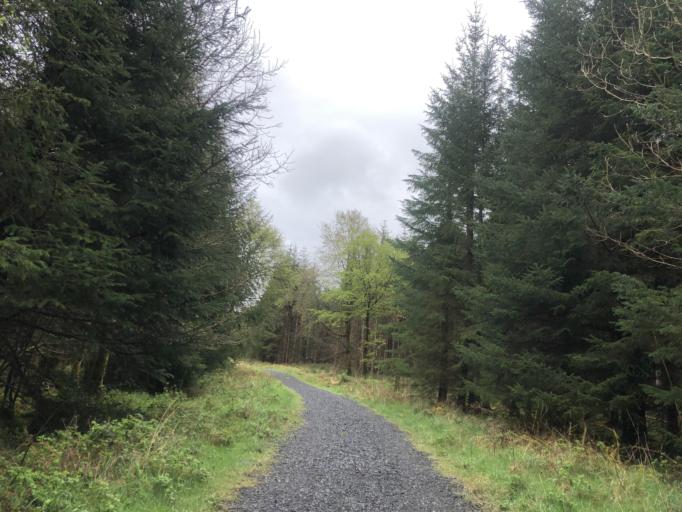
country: IE
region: Connaught
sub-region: Roscommon
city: Boyle
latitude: 53.9837
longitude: -8.1935
